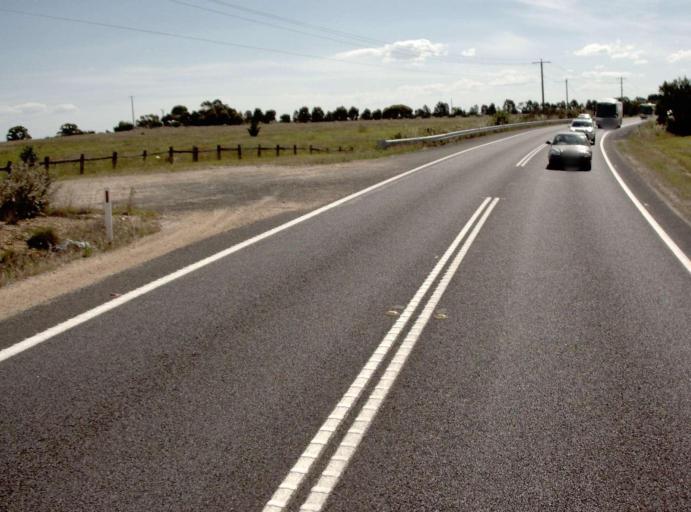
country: AU
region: Victoria
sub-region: East Gippsland
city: Bairnsdale
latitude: -37.8265
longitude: 147.7139
